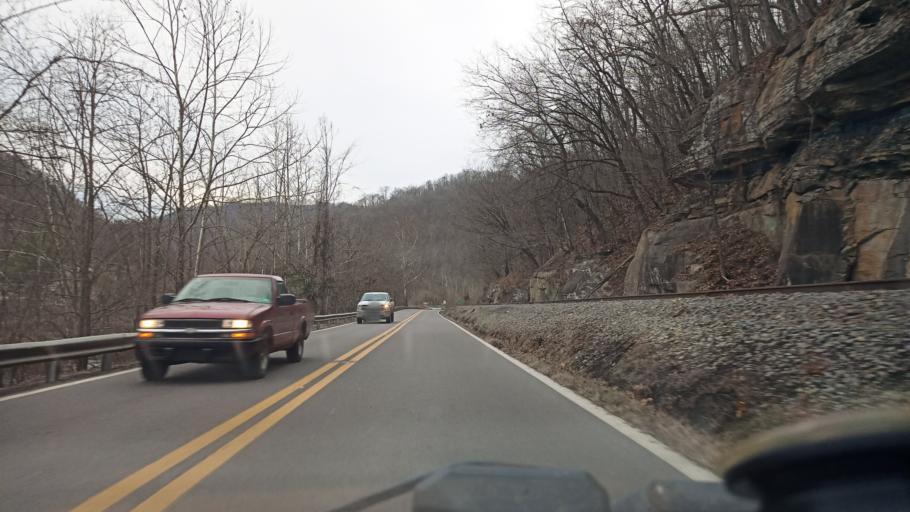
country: US
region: West Virginia
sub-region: Logan County
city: Mallory
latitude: 37.6931
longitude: -81.8631
